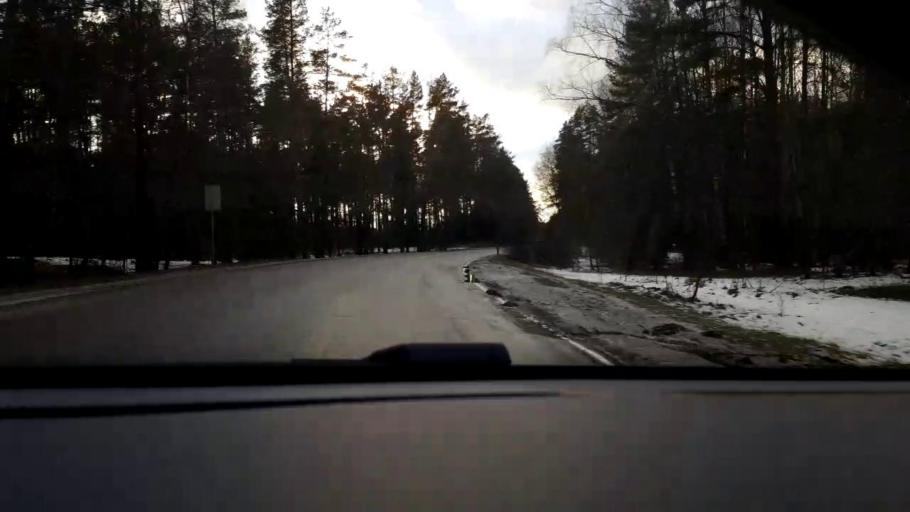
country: LT
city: Nemencine
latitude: 54.8029
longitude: 25.4076
